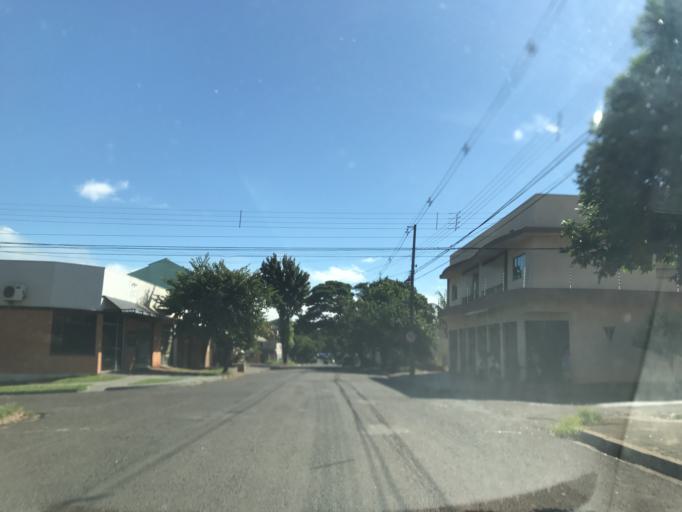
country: BR
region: Parana
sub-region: Maringa
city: Maringa
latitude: -23.4549
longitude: -51.9608
